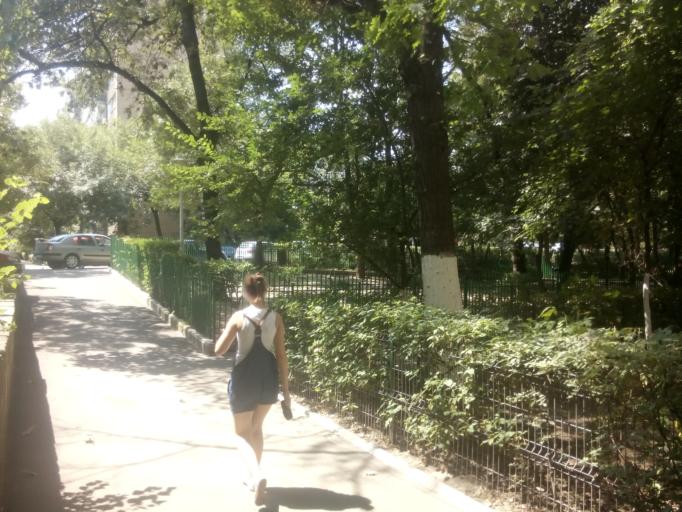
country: RO
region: Ilfov
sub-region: Comuna Fundeni-Dobroesti
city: Fundeni
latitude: 44.4290
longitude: 26.1481
